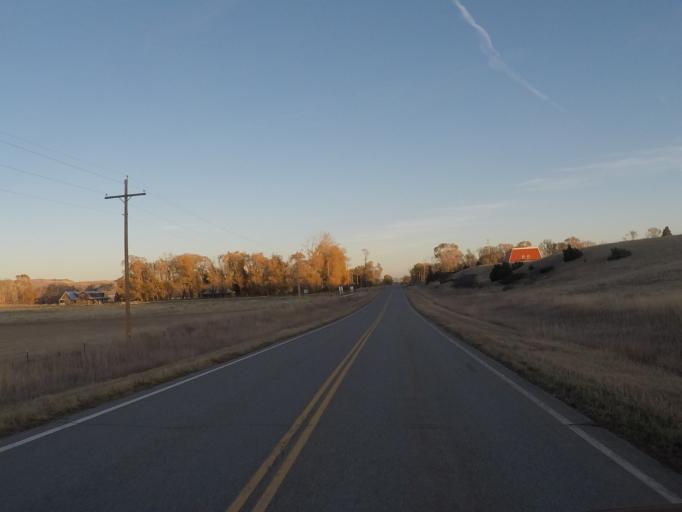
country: US
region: Montana
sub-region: Sweet Grass County
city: Big Timber
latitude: 45.7775
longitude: -109.8103
